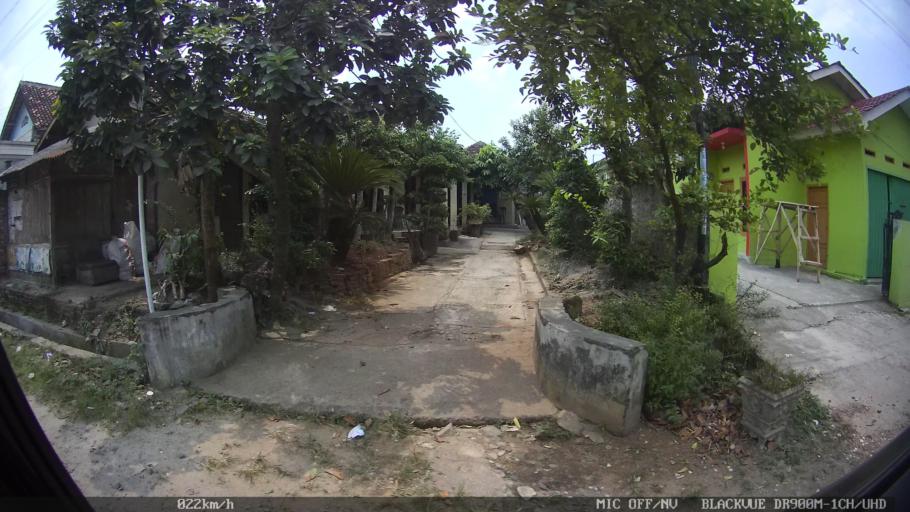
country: ID
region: Lampung
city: Pringsewu
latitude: -5.3505
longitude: 104.9709
